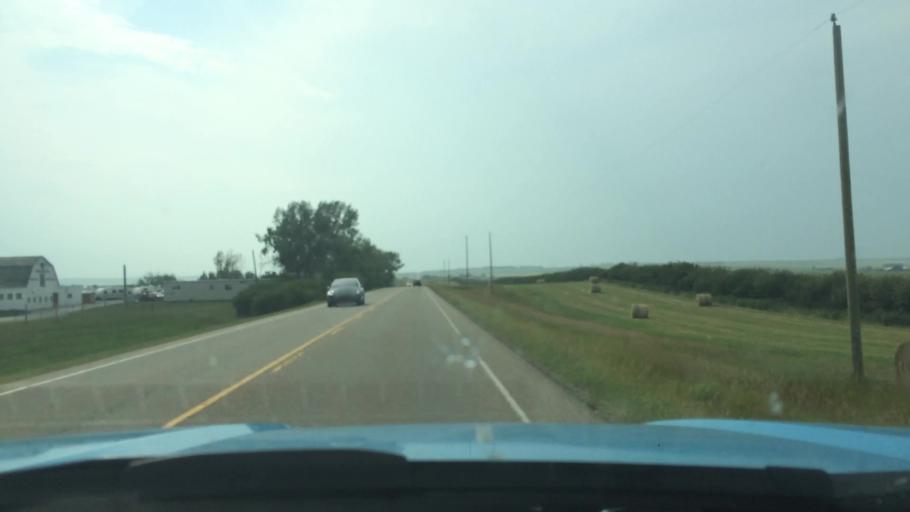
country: CA
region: Alberta
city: Airdrie
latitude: 51.2126
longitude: -114.0540
